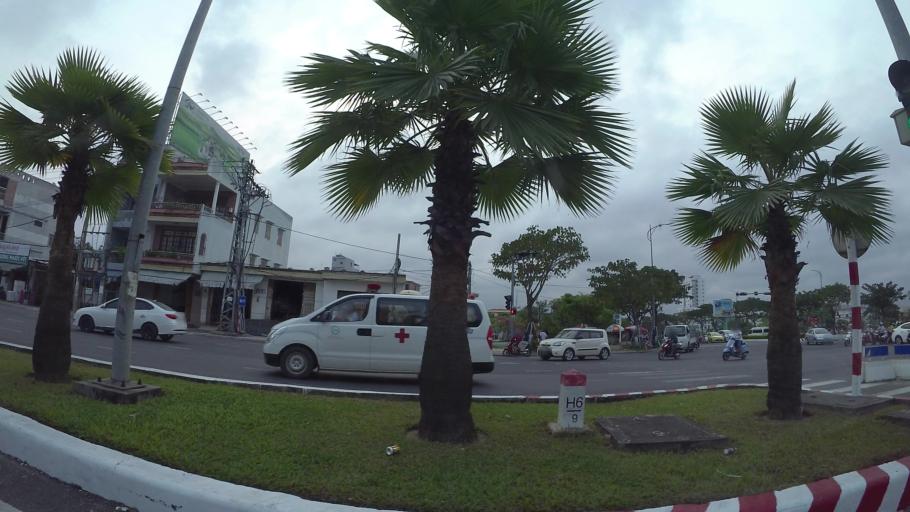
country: VN
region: Da Nang
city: Son Tra
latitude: 16.0610
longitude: 108.2345
